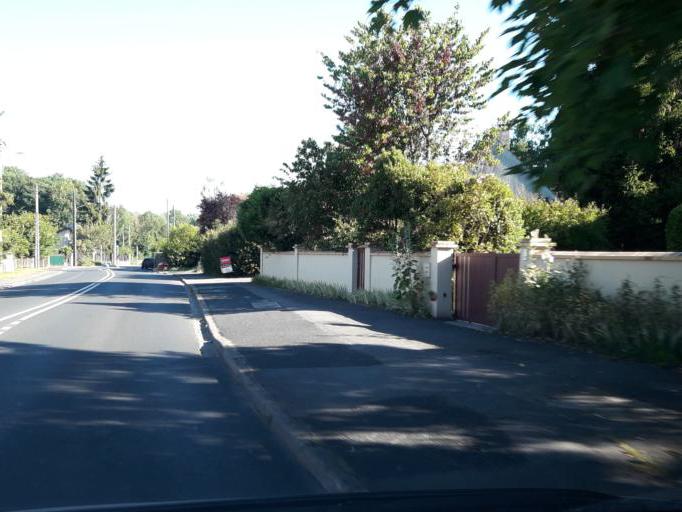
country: FR
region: Ile-de-France
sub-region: Departement de l'Essonne
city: Saint-Vrain
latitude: 48.5302
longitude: 2.3401
